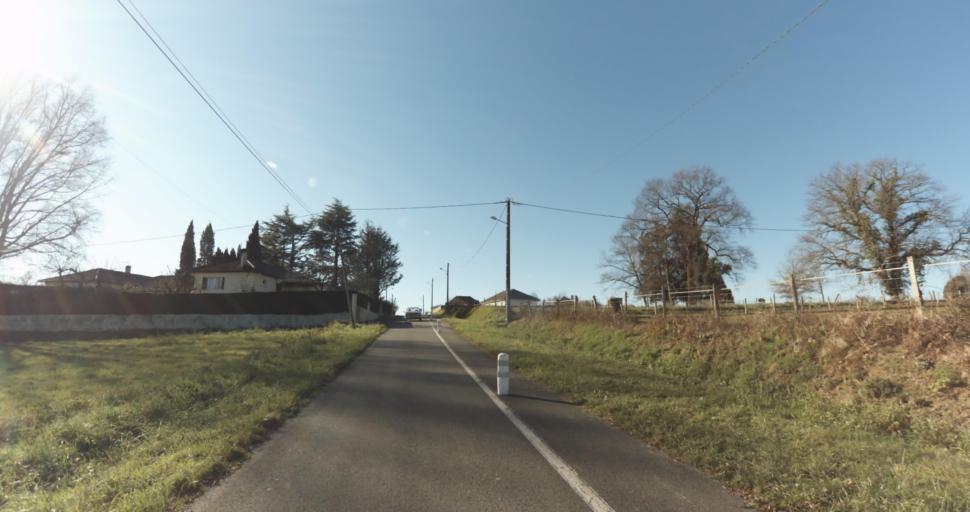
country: FR
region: Aquitaine
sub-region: Departement des Pyrenees-Atlantiques
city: Morlaas
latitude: 43.3392
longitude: -0.2702
